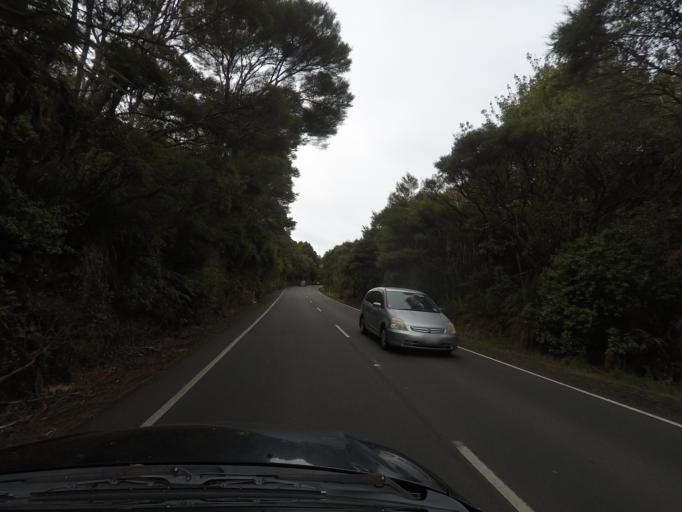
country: NZ
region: Auckland
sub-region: Auckland
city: Titirangi
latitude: -36.9335
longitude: 174.5670
